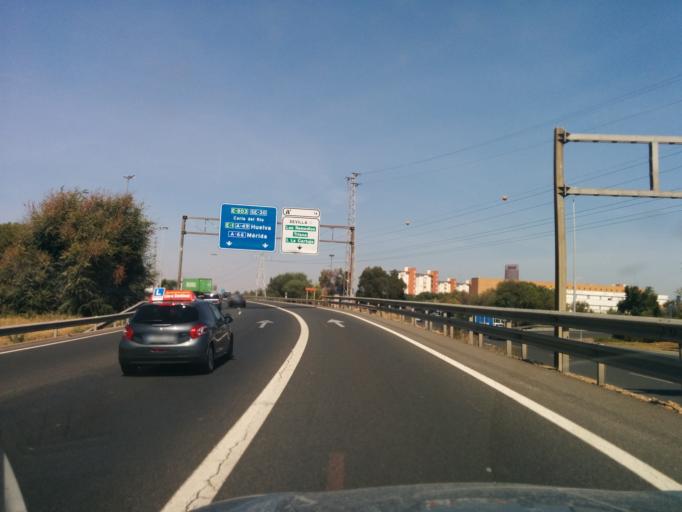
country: ES
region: Andalusia
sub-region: Provincia de Sevilla
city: San Juan de Aznalfarache
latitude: 37.3711
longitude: -6.0138
